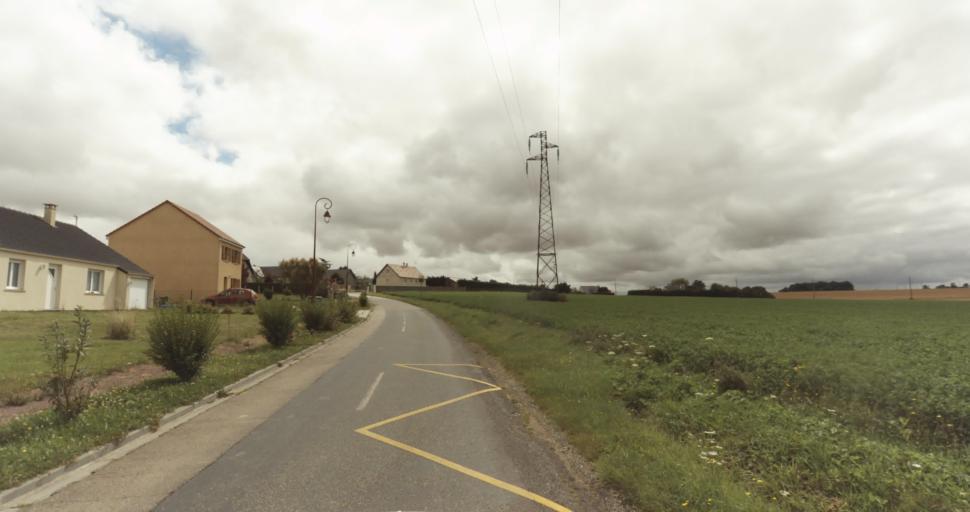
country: FR
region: Haute-Normandie
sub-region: Departement de l'Eure
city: Evreux
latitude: 48.9395
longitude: 1.1918
